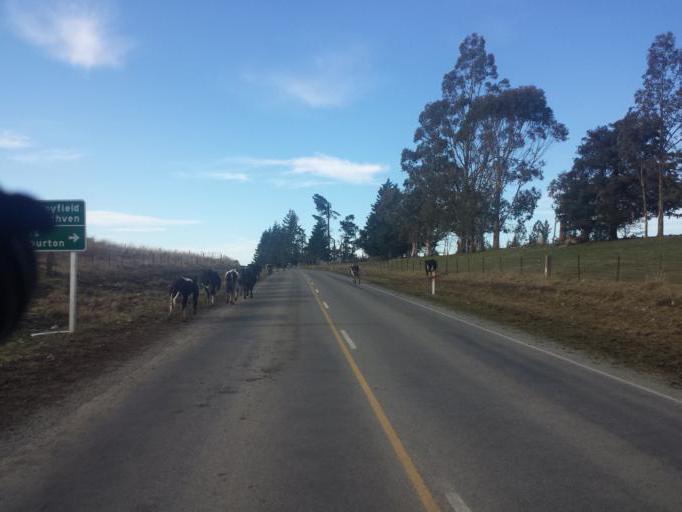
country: NZ
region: Canterbury
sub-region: Timaru District
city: Pleasant Point
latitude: -43.9719
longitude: 171.3082
